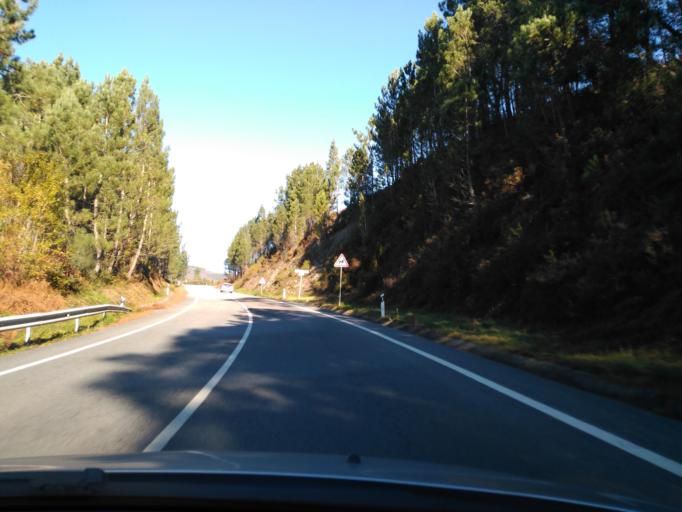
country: PT
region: Braga
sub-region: Cabeceiras de Basto
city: Cabeceiras de Basto
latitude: 41.6868
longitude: -7.9535
